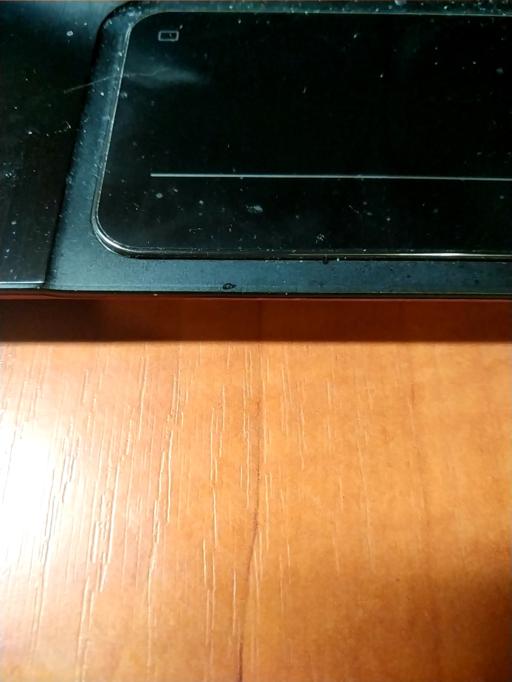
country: RU
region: Tverskaya
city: Ves'yegonsk
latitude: 58.7295
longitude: 37.5438
